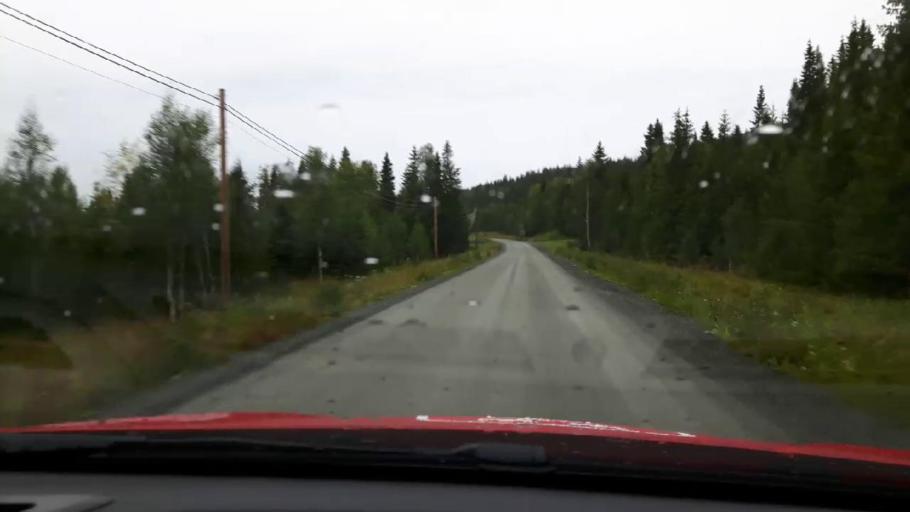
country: SE
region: Jaemtland
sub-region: Are Kommun
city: Are
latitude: 63.4812
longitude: 12.7963
